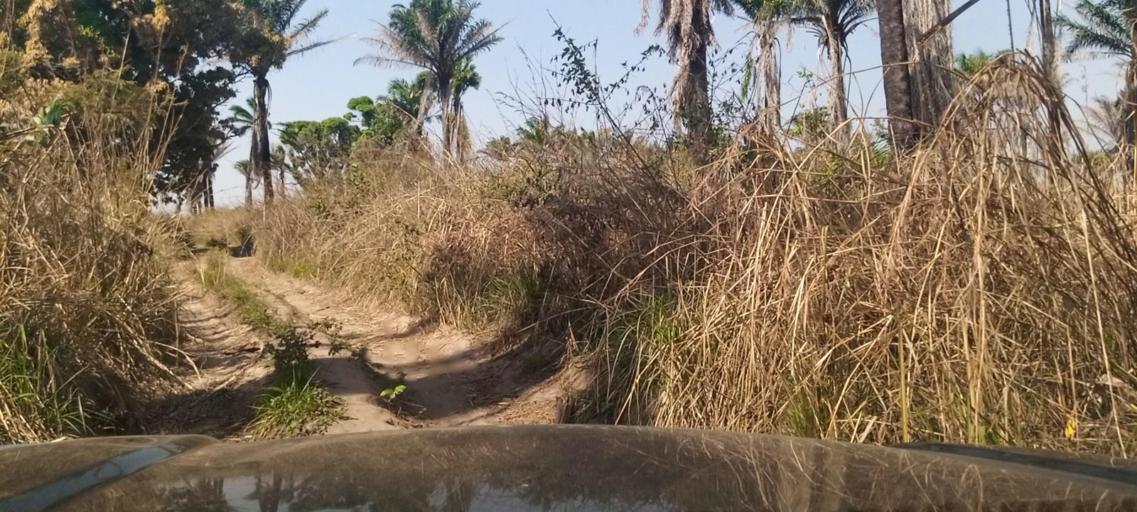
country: CD
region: Kasai-Oriental
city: Kabinda
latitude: -5.7793
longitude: 25.0665
